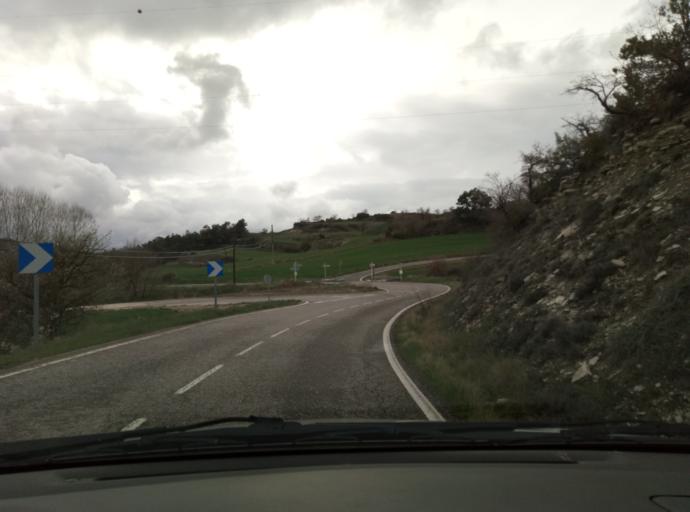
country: ES
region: Catalonia
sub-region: Provincia de Tarragona
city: Santa Coloma de Queralt
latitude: 41.5412
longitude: 1.3467
